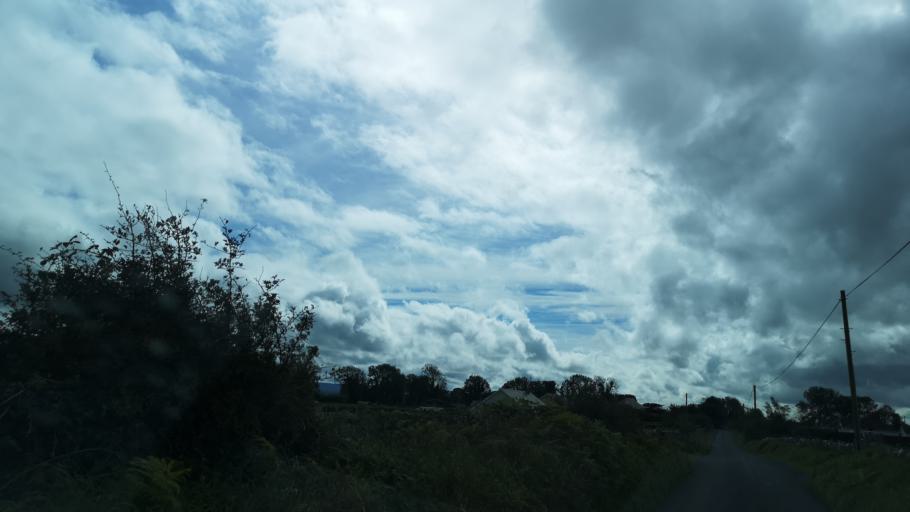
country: IE
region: Connaught
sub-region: County Galway
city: Athenry
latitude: 53.2800
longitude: -8.6695
